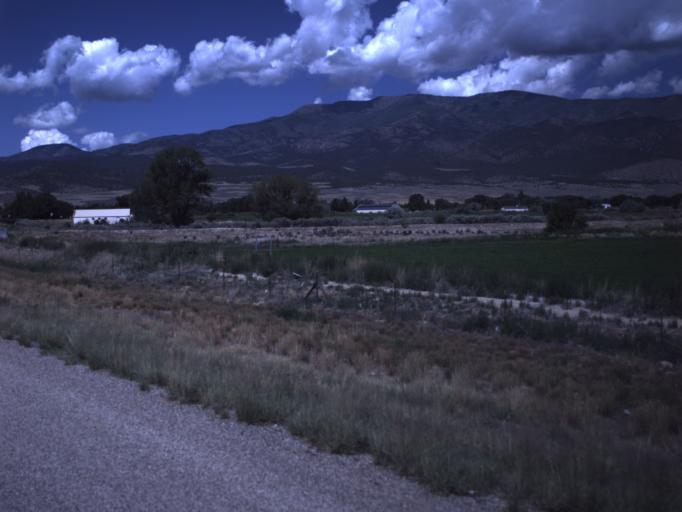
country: US
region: Utah
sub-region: Piute County
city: Junction
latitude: 38.1724
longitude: -112.2597
